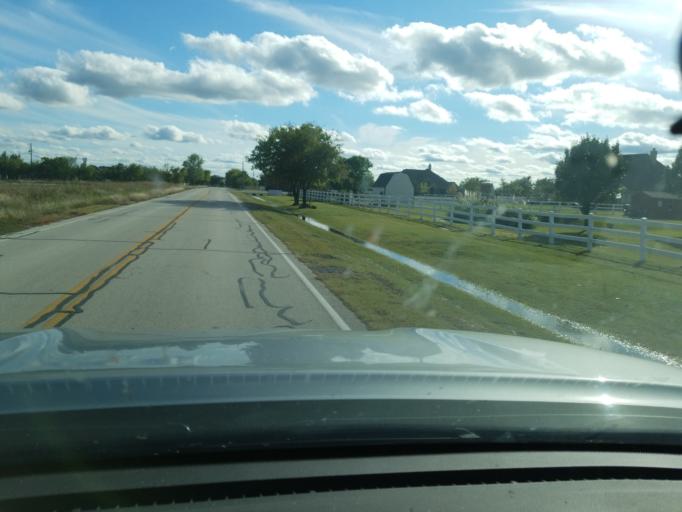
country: US
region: Texas
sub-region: Tarrant County
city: Pecan Acres
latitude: 32.9865
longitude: -97.4164
